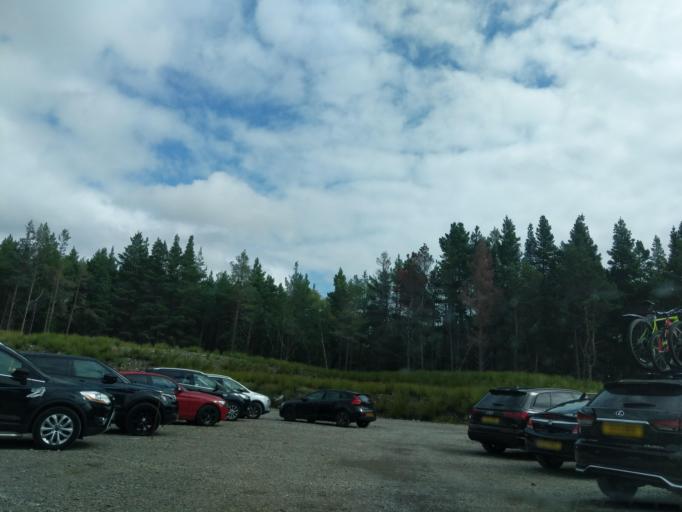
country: GB
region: Scotland
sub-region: Highland
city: Aviemore
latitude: 57.2791
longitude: -3.8179
